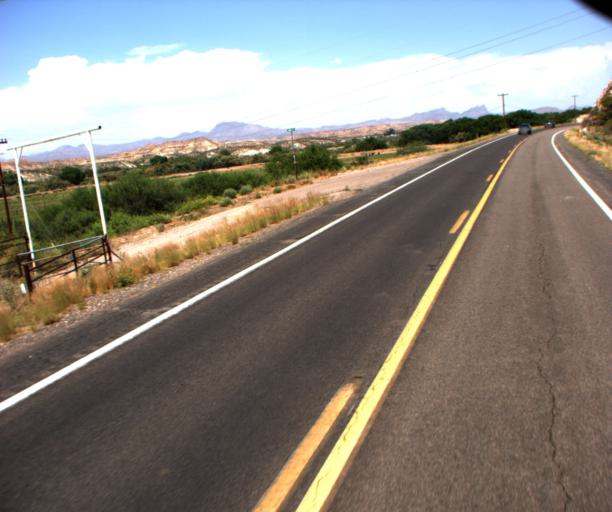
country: US
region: Arizona
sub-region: Greenlee County
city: Clifton
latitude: 32.7416
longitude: -109.1340
